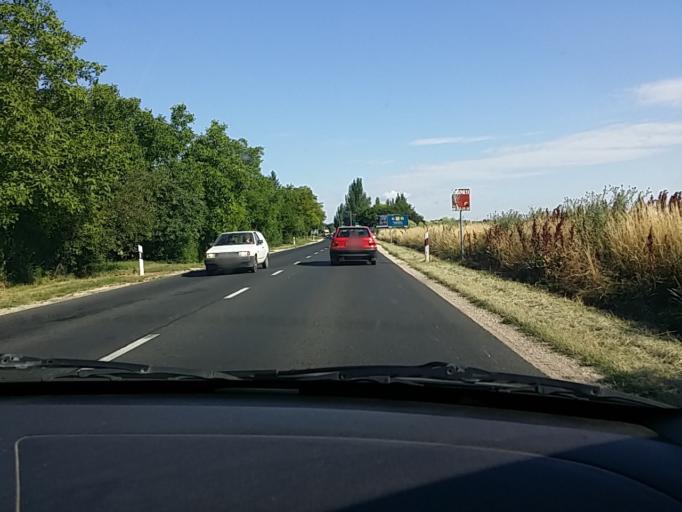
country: HU
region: Veszprem
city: Balatonkenese
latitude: 47.0107
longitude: 18.1721
